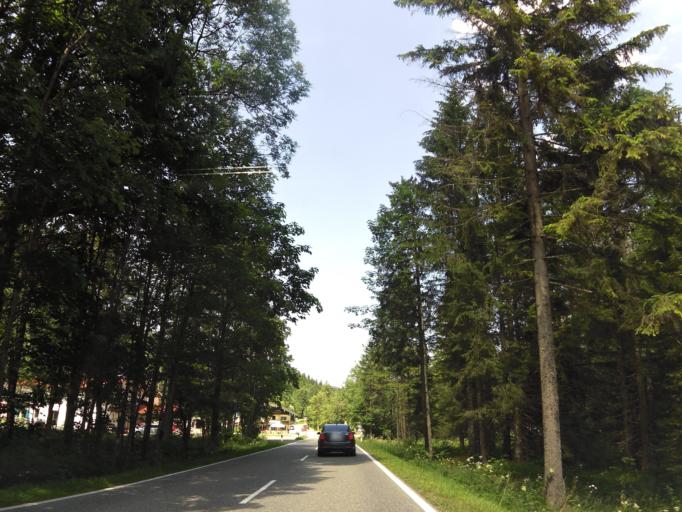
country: DE
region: Bavaria
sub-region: Upper Bavaria
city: Ruhpolding
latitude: 47.7244
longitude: 12.6575
